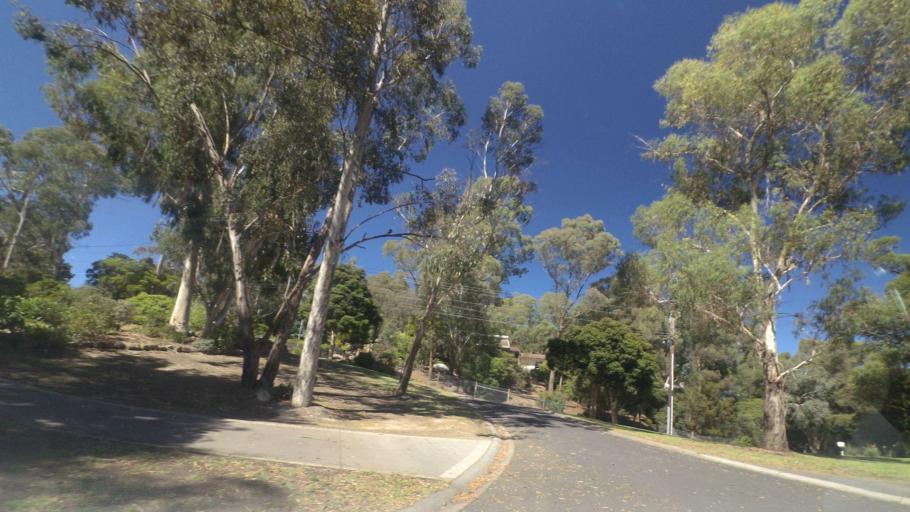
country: AU
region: Victoria
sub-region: Manningham
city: Donvale
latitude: -37.7917
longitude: 145.1924
